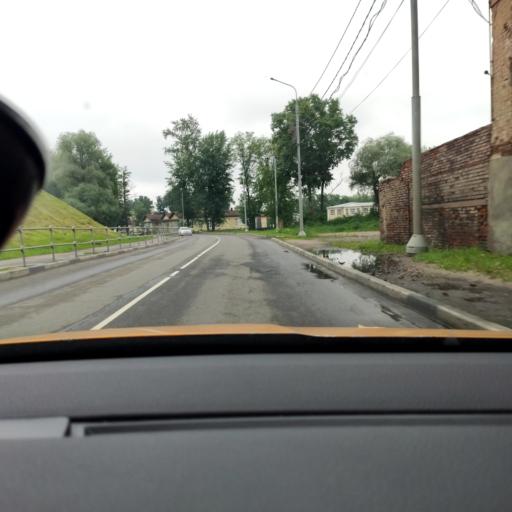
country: RU
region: Moskovskaya
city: Serpukhov
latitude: 54.9144
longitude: 37.4053
